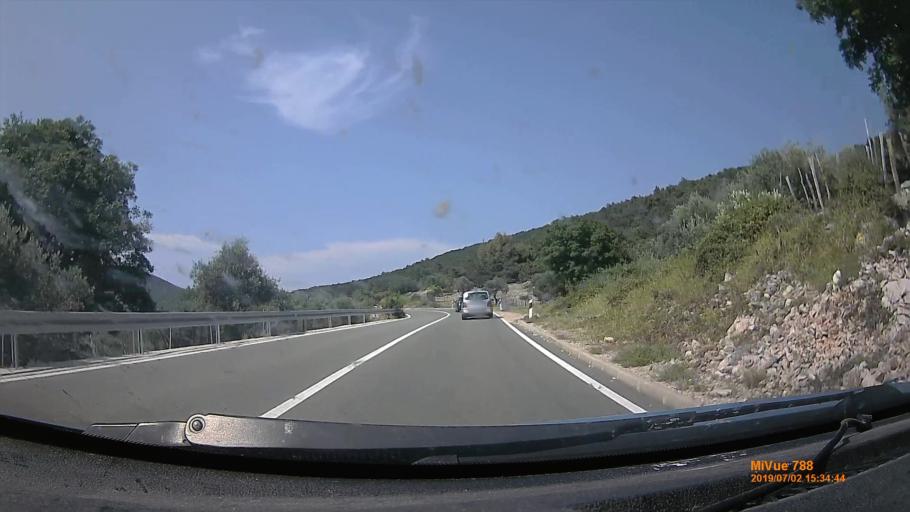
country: HR
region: Primorsko-Goranska
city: Cres
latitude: 44.9701
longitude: 14.4125
